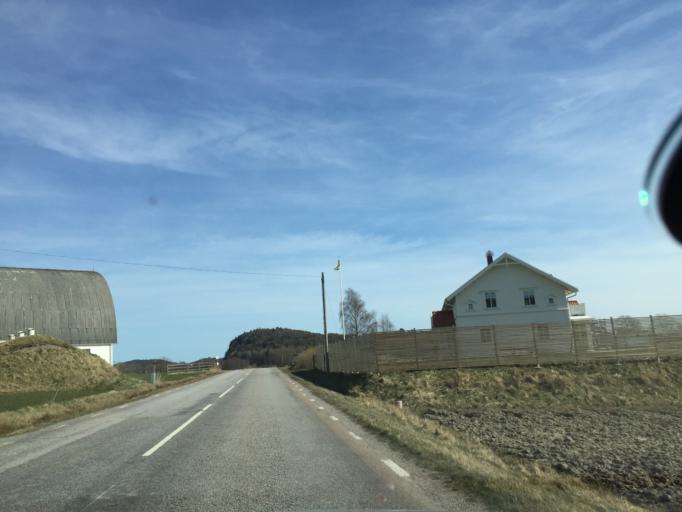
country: SE
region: Vaestra Goetaland
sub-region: Orust
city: Henan
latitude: 58.3425
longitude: 11.7381
